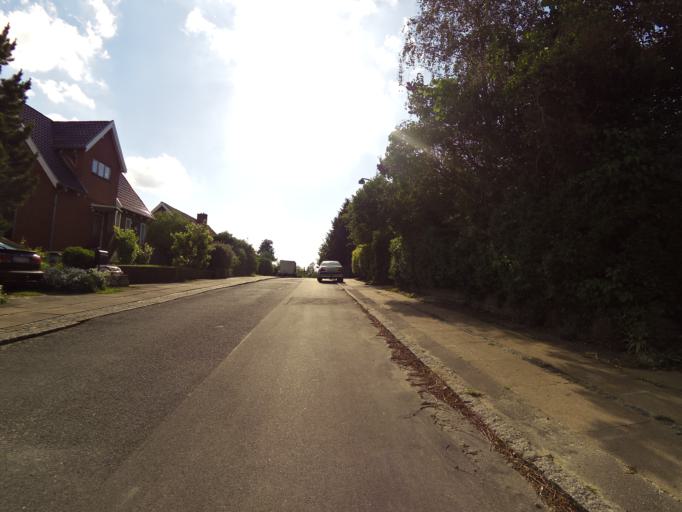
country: DK
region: Capital Region
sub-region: Lyngby-Tarbaek Kommune
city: Kongens Lyngby
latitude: 55.7440
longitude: 12.5268
